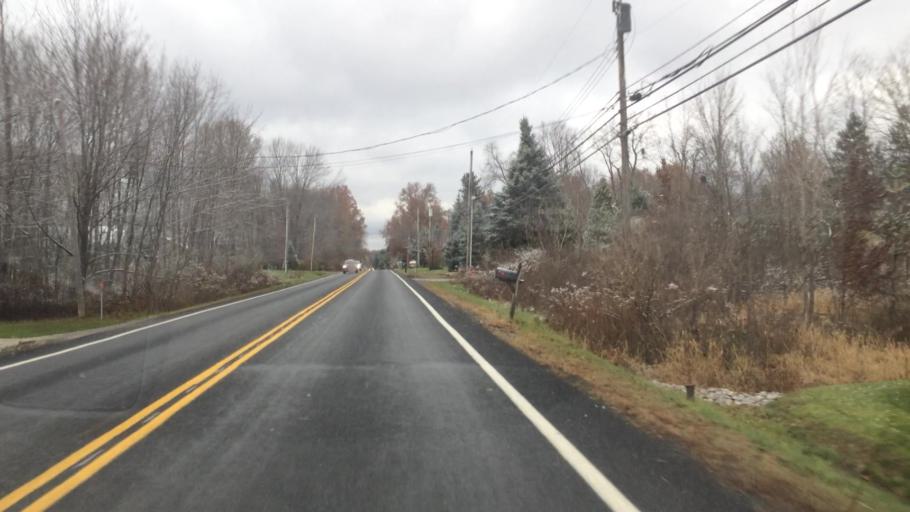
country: US
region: Ohio
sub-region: Summit County
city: Boston Heights
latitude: 41.2875
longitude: -81.5181
